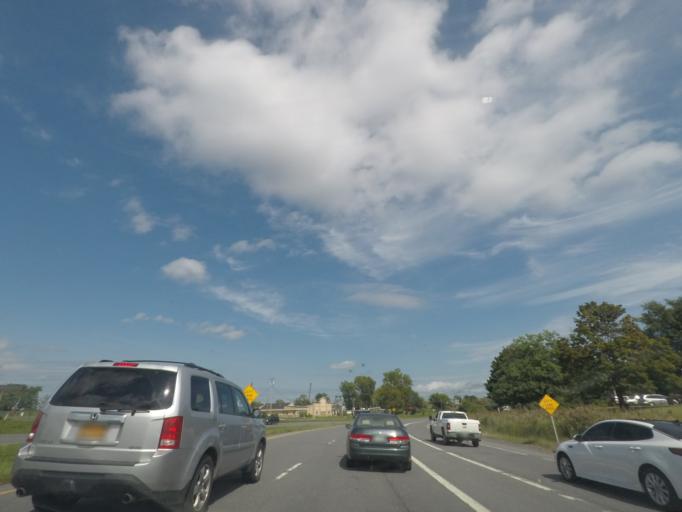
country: US
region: New York
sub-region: Albany County
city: Albany
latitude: 42.6189
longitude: -73.7836
